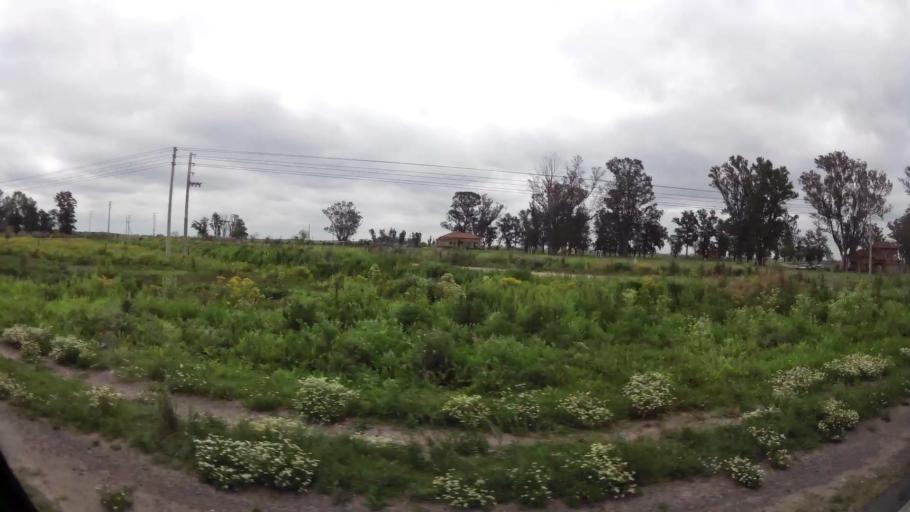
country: AR
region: Buenos Aires
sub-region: Partido de San Vicente
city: San Vicente
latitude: -34.9766
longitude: -58.4679
